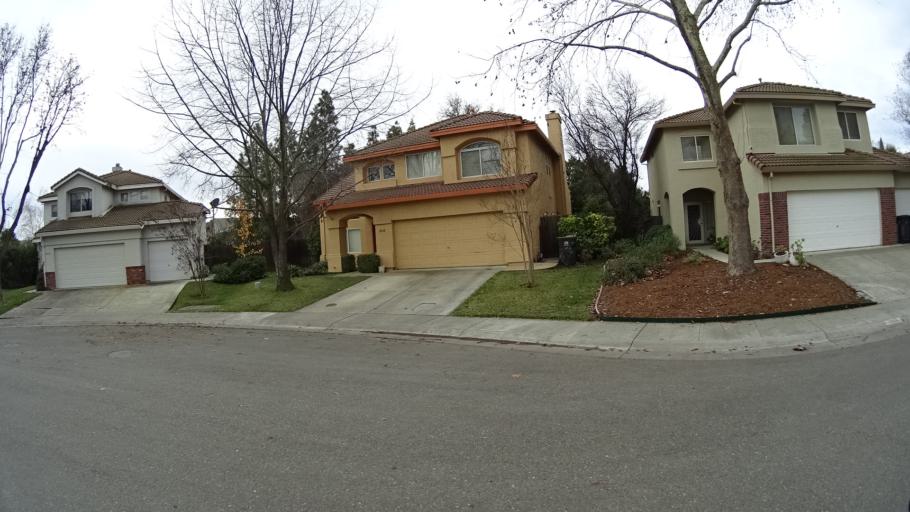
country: US
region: California
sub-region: Yolo County
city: Davis
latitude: 38.5534
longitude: -121.7157
